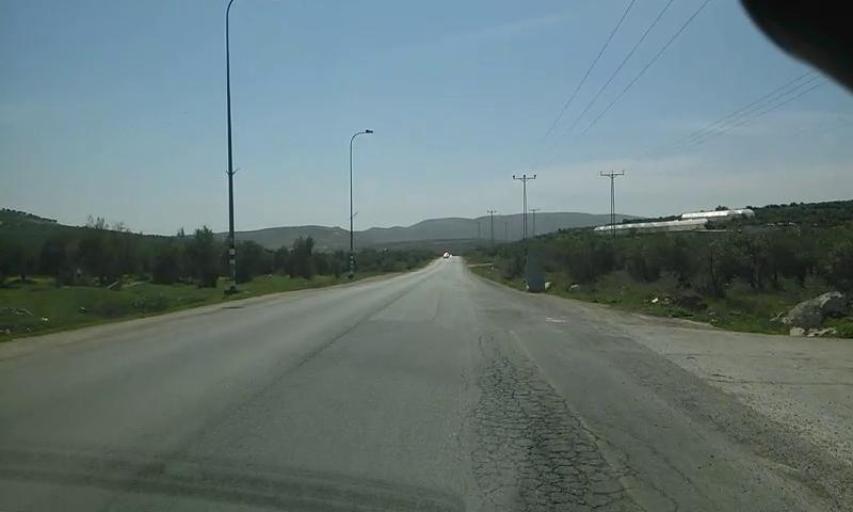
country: PS
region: West Bank
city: Marah Rabbah
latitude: 31.6383
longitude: 35.2026
